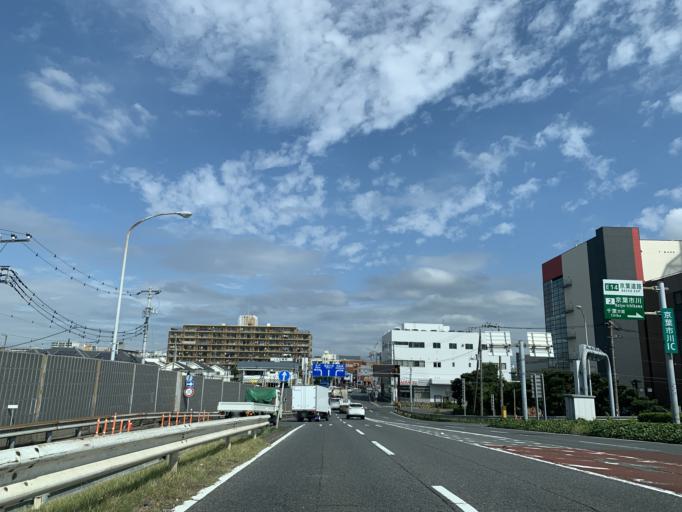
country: JP
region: Tokyo
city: Urayasu
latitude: 35.7102
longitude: 139.9263
